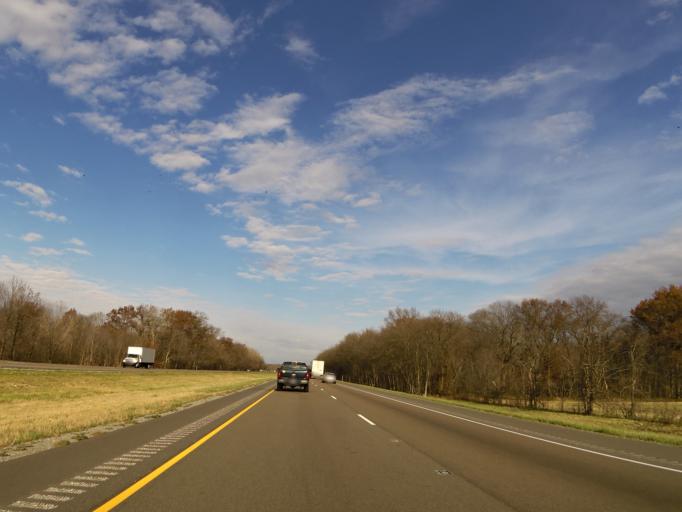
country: US
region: Illinois
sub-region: Washington County
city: Okawville
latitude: 38.4665
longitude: -89.5714
